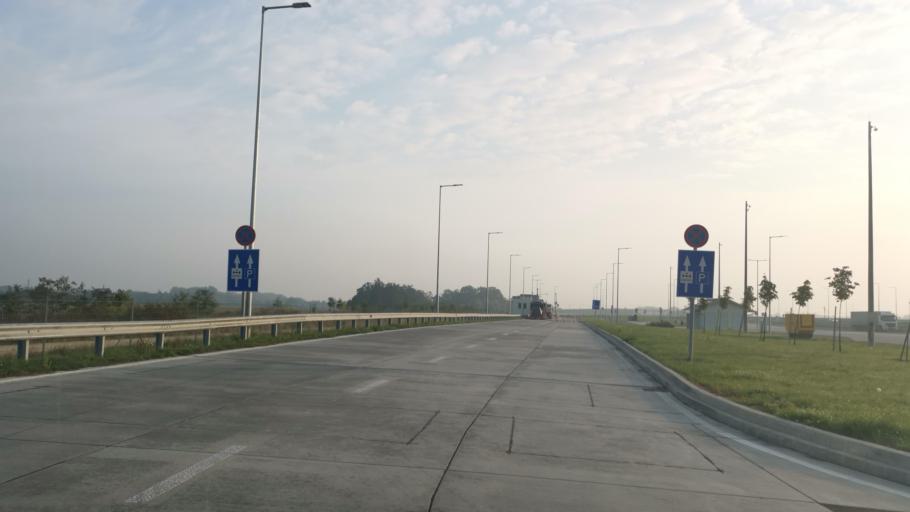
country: HU
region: Vas
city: Repcelak
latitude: 47.3849
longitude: 16.9713
